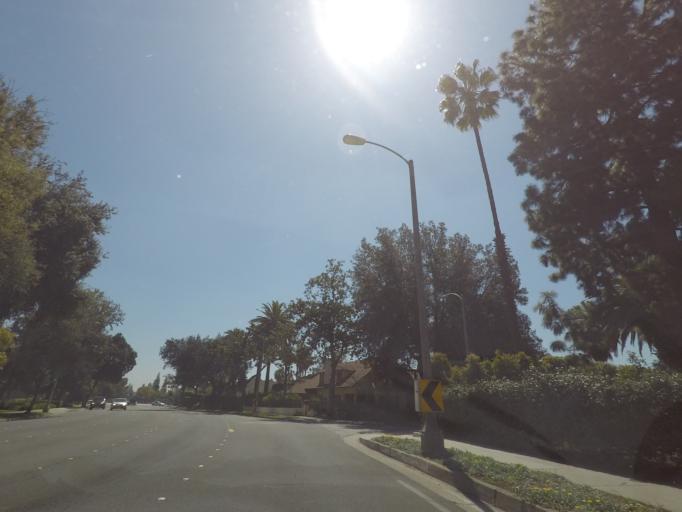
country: US
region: California
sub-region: Los Angeles County
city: Pasadena
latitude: 34.1487
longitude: -118.1618
